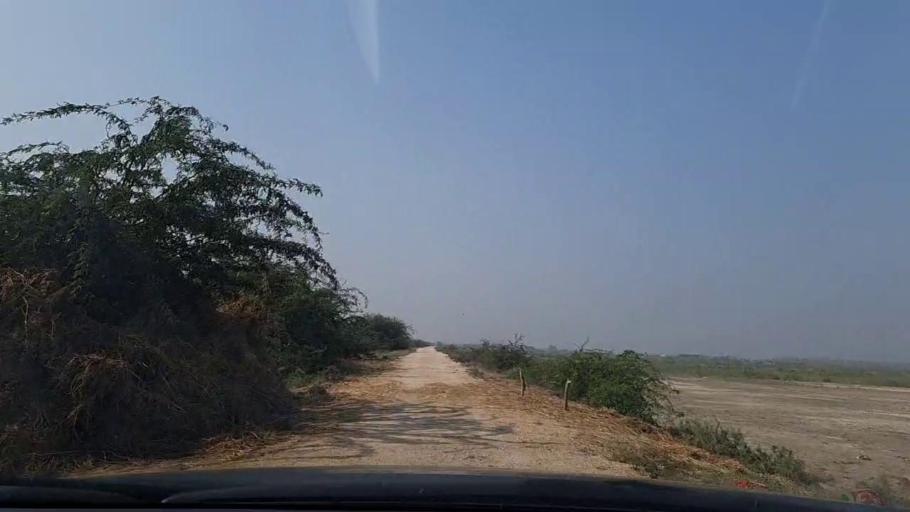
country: PK
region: Sindh
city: Mirpur Sakro
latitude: 24.5750
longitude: 67.7645
